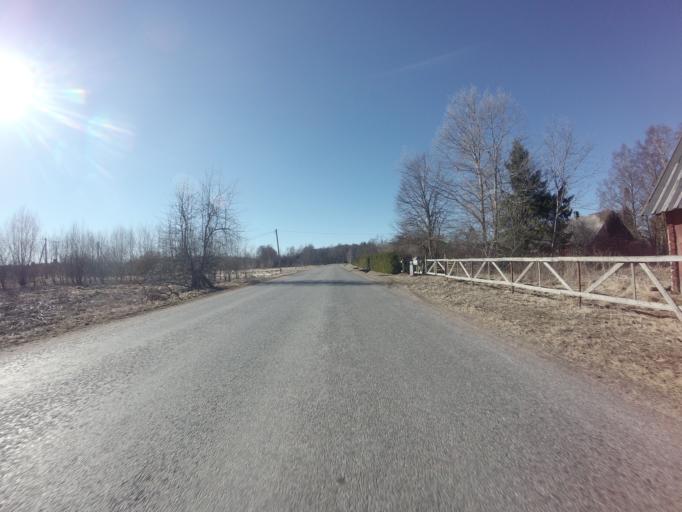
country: EE
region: Saare
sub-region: Kuressaare linn
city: Kuressaare
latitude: 58.5748
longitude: 22.6495
